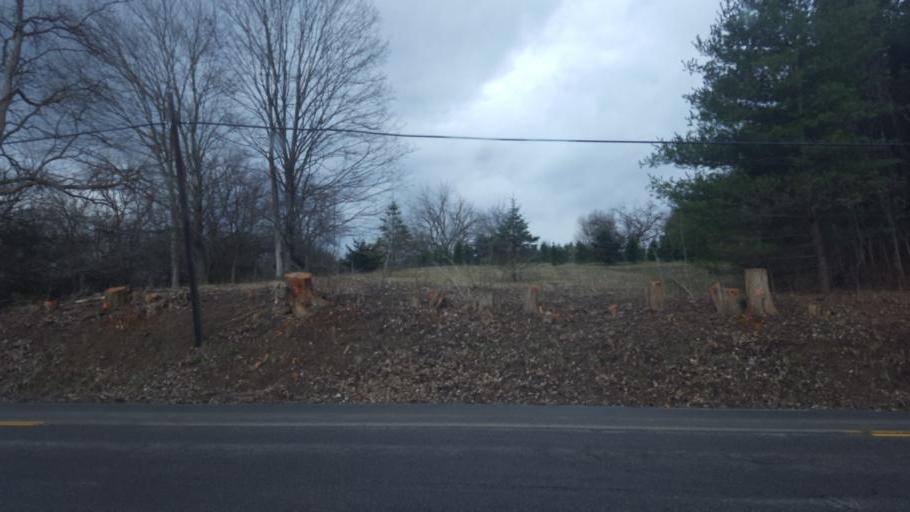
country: US
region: Ohio
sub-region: Delaware County
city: Lewis Center
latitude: 40.1767
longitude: -82.9626
